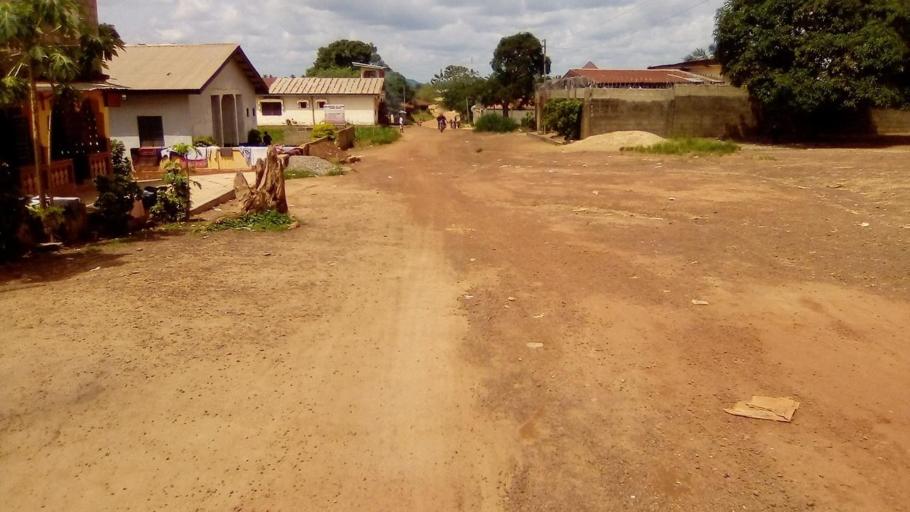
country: SL
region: Southern Province
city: Bo
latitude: 7.9672
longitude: -11.7258
